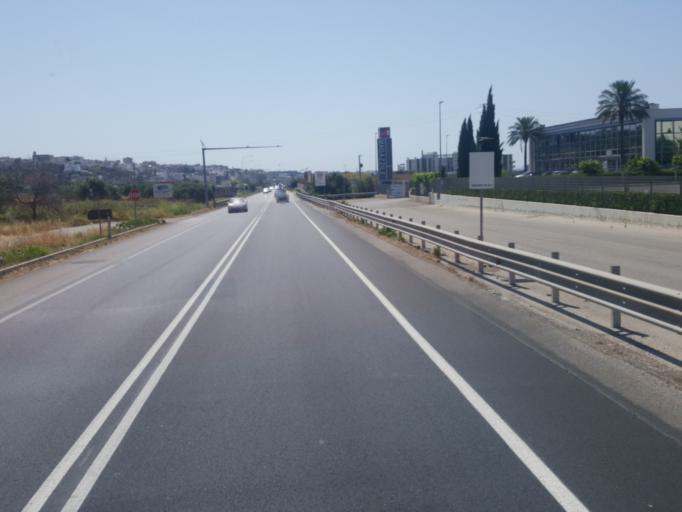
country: IT
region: Apulia
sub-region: Provincia di Taranto
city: Massafra
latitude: 40.5915
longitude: 17.0961
